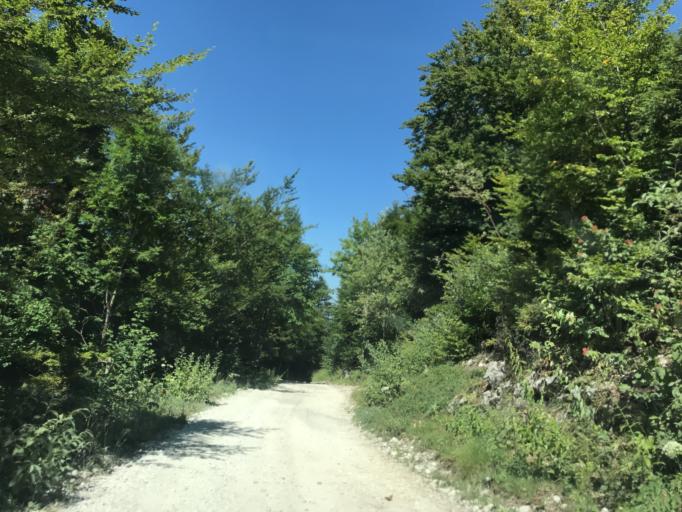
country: FR
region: Rhone-Alpes
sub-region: Departement de la Haute-Savoie
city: Thorens-Glieres
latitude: 45.9727
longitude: 6.2395
